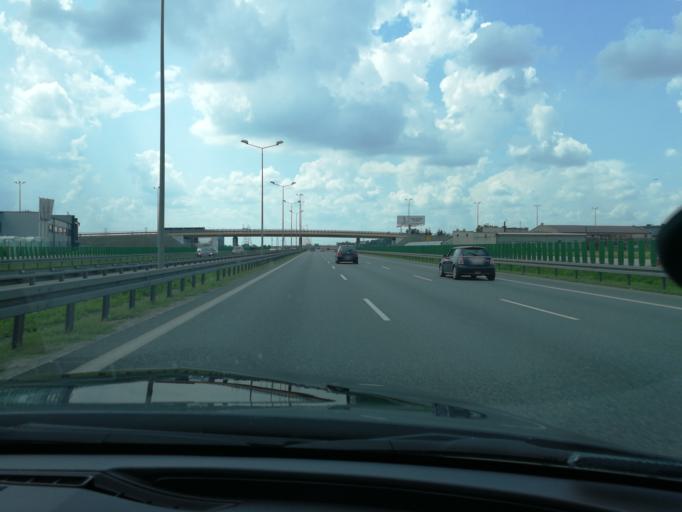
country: PL
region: Masovian Voivodeship
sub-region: Powiat warszawski zachodni
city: Babice
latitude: 52.2297
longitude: 20.8781
